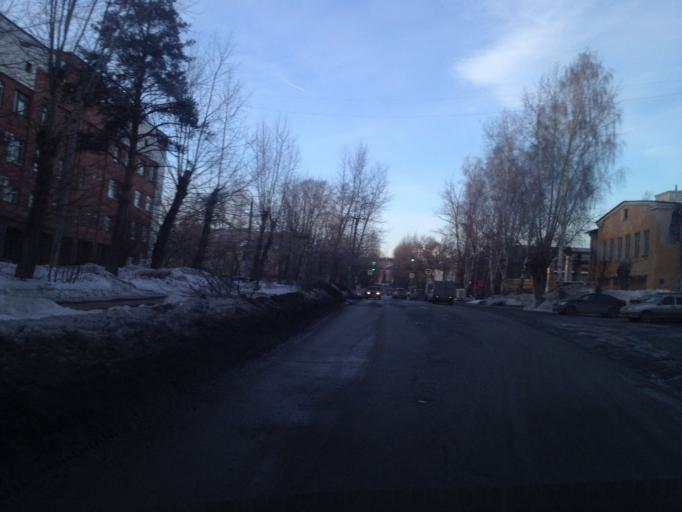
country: RU
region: Sverdlovsk
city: Istok
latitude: 56.7576
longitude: 60.7104
